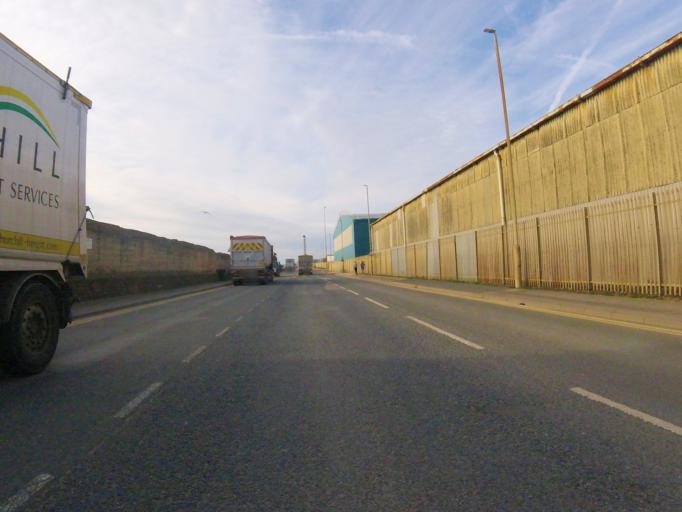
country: GB
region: England
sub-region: East Sussex
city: Portslade
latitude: 50.8276
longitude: -0.2139
